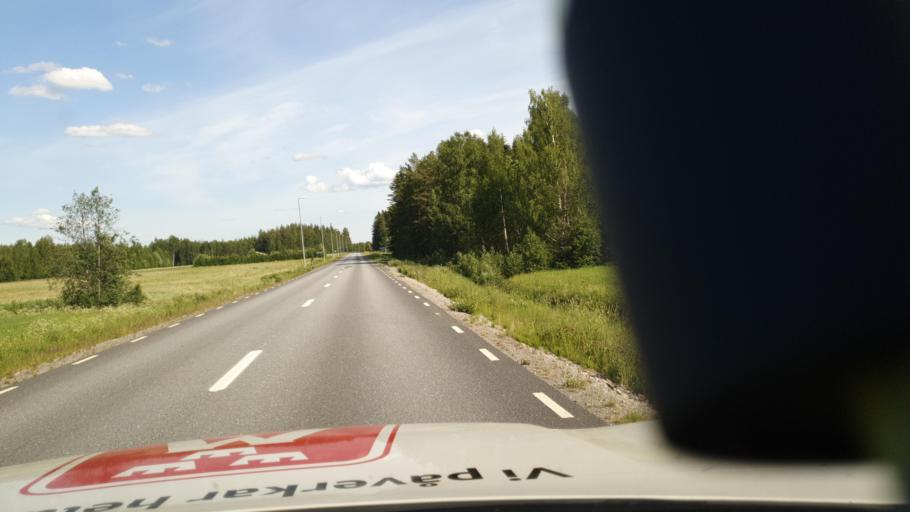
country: SE
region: Vaesterbotten
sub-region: Skelleftea Kommun
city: Forsbacka
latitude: 64.6961
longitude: 20.4844
